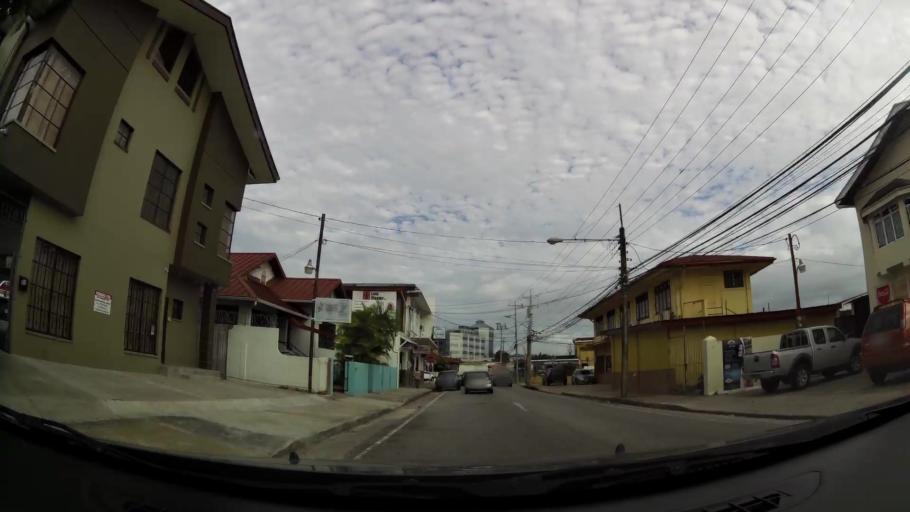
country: TT
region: City of Port of Spain
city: Port-of-Spain
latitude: 10.6654
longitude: -61.5246
